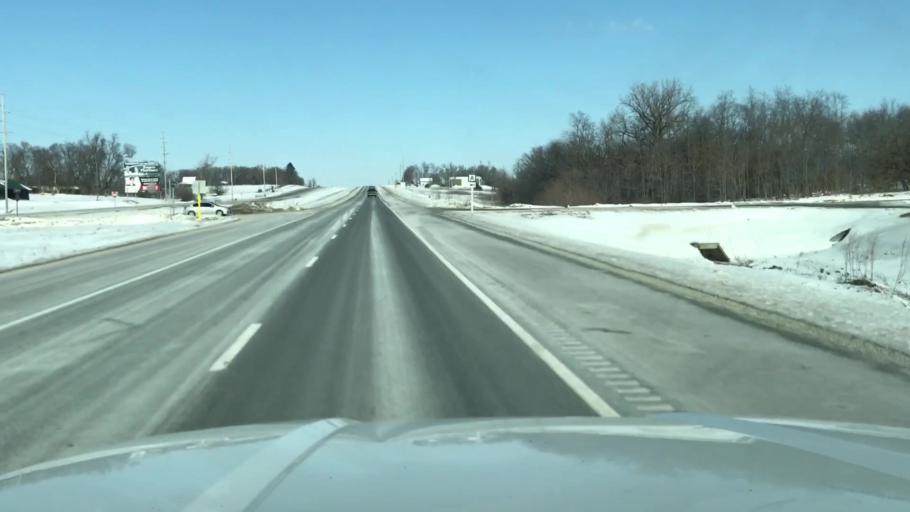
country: US
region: Missouri
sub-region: Nodaway County
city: Maryville
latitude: 40.1996
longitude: -94.8676
